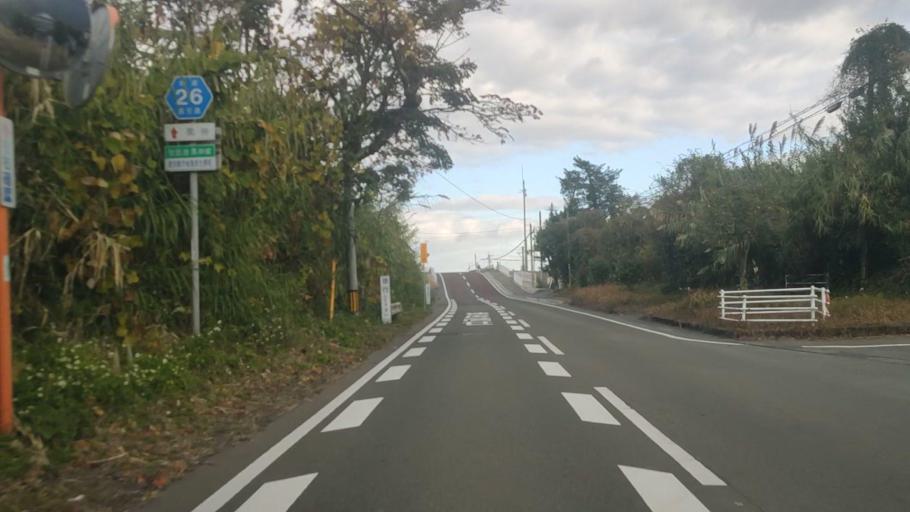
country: JP
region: Kagoshima
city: Kagoshima-shi
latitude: 31.6072
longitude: 130.6121
